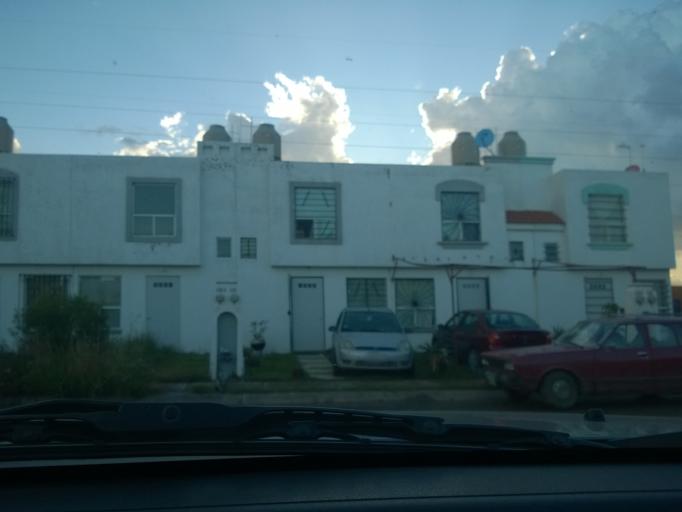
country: MX
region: Guanajuato
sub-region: Leon
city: Fraccionamiento Paraiso Real
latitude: 21.1063
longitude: -101.5979
